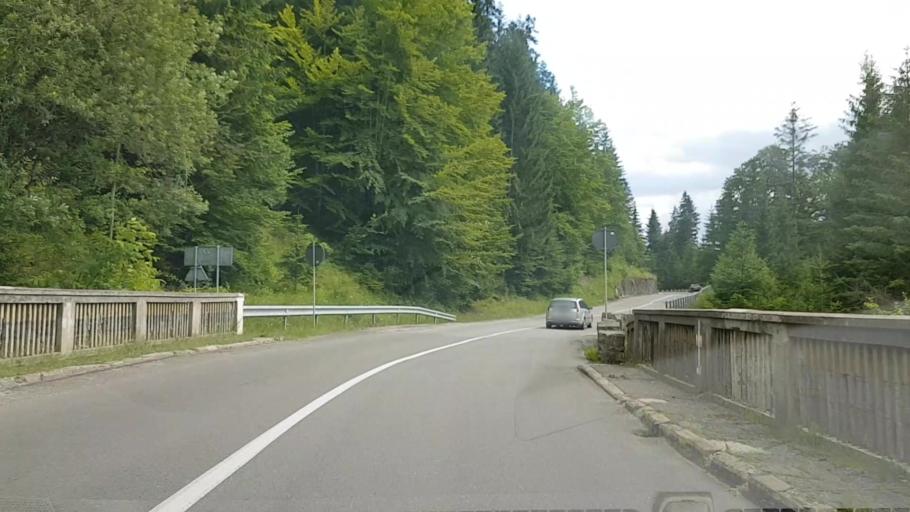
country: RO
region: Neamt
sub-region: Comuna Pangarati
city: Pangarati
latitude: 46.9751
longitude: 26.1170
